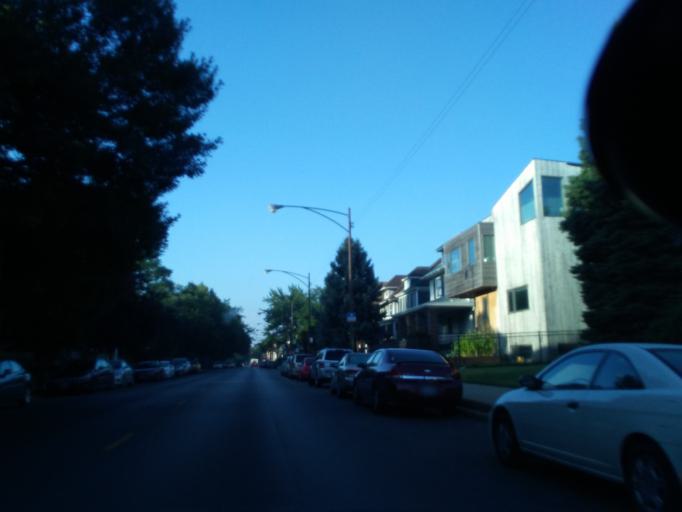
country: US
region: Illinois
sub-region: Cook County
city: Lincolnwood
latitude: 41.9273
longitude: -87.7122
